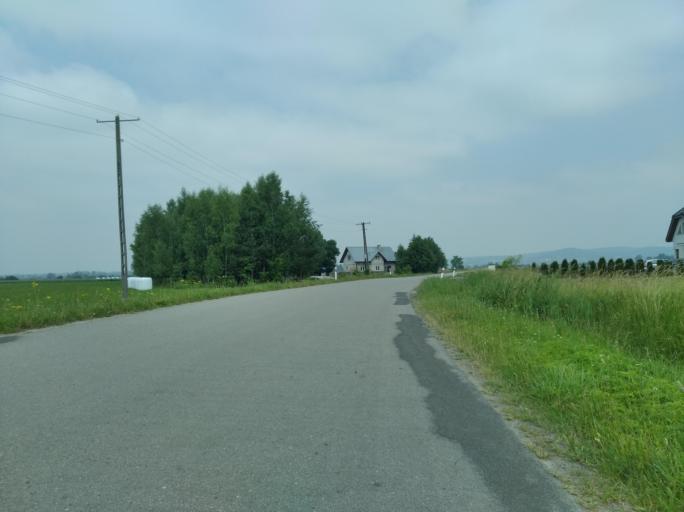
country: PL
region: Subcarpathian Voivodeship
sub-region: Powiat sanocki
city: Besko
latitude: 49.6057
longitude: 21.9560
